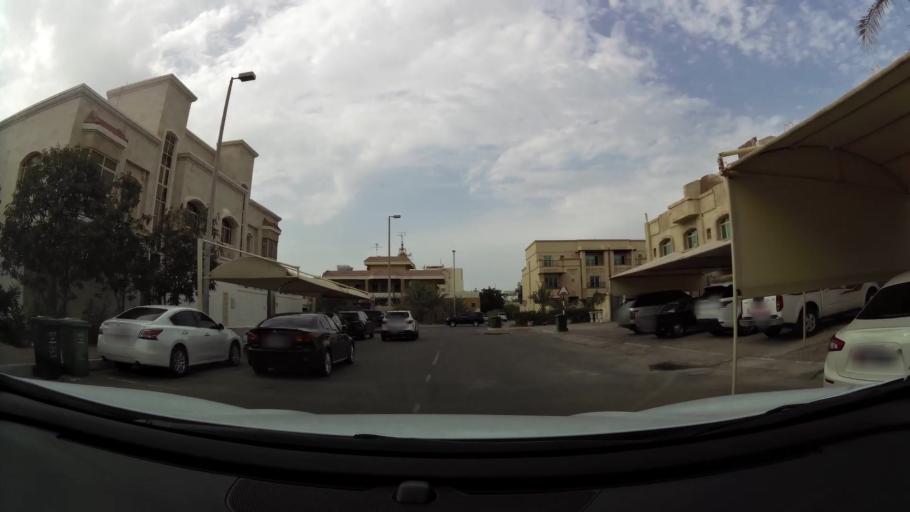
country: AE
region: Abu Dhabi
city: Abu Dhabi
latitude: 24.4596
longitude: 54.3538
